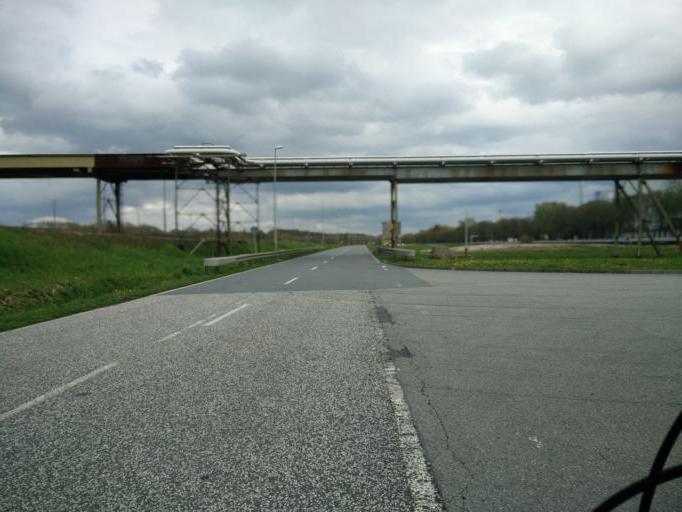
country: DE
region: Mecklenburg-Vorpommern
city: Nienhagen
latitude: 54.1463
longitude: 12.1385
